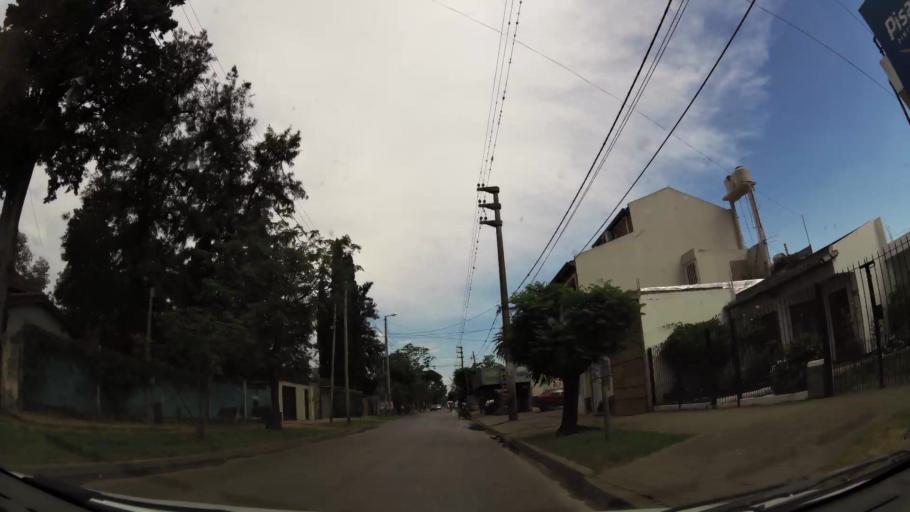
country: AR
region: Buenos Aires
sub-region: Partido de Merlo
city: Merlo
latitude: -34.6321
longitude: -58.6994
